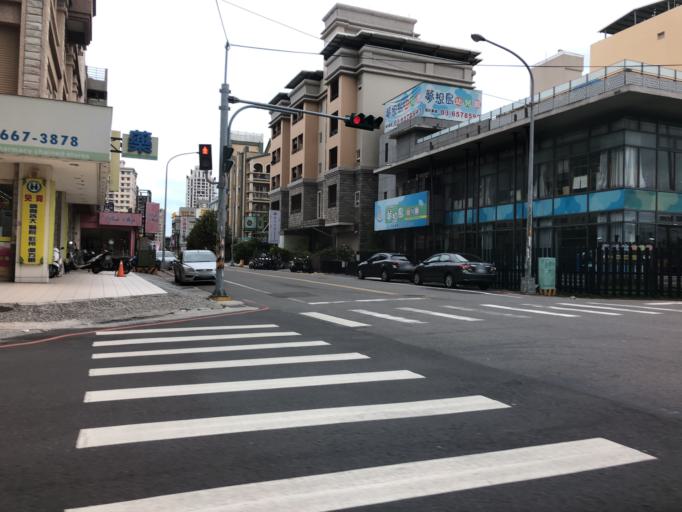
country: TW
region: Taiwan
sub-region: Hsinchu
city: Zhubei
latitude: 24.8222
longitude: 121.0279
